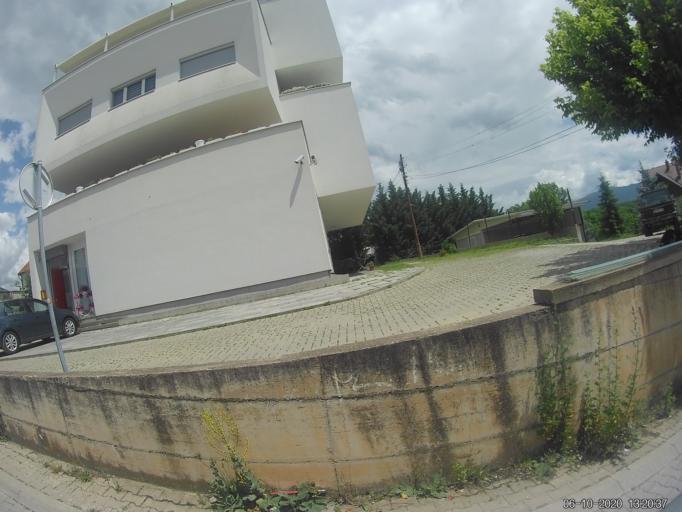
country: XK
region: Prizren
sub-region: Komuna e Therandes
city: Suva Reka
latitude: 42.3592
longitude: 20.8287
